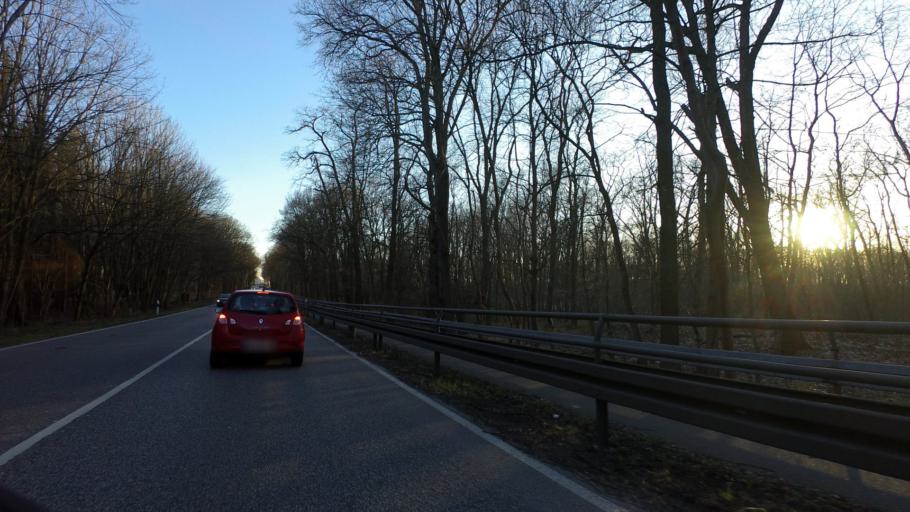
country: DE
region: Brandenburg
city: Ahrensfelde
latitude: 52.5924
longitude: 13.5956
